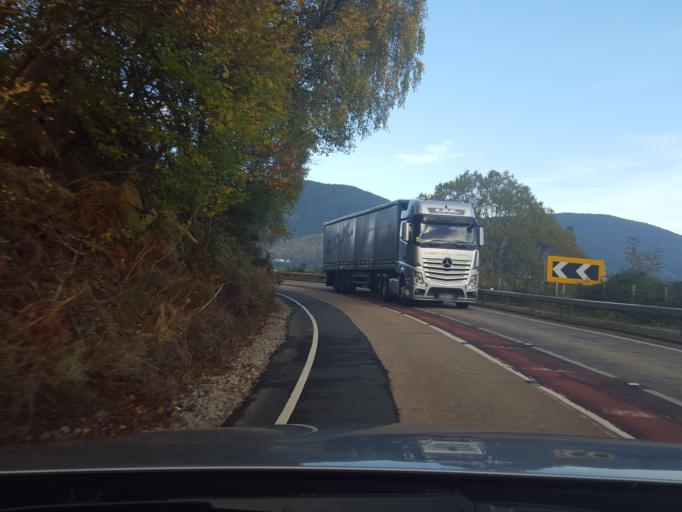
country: GB
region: Scotland
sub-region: Highland
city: Beauly
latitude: 57.3263
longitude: -4.4452
